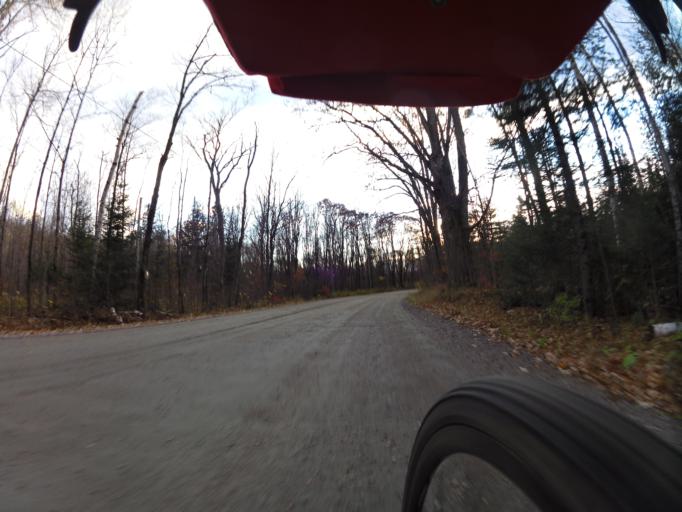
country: CA
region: Quebec
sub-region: Outaouais
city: Shawville
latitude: 45.6624
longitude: -76.3014
